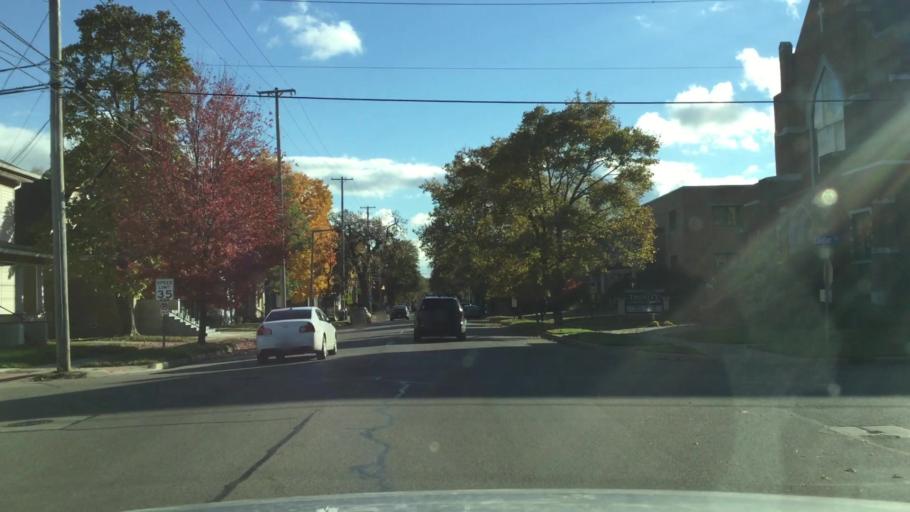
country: US
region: Michigan
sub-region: Kalamazoo County
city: Kalamazoo
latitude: 42.2876
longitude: -85.5896
